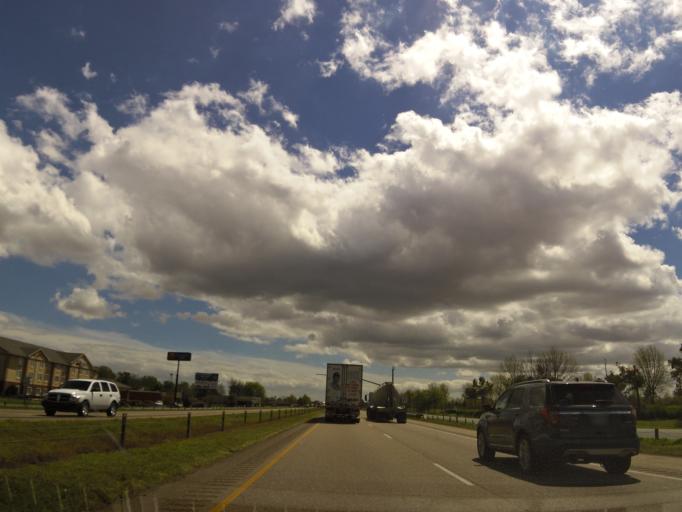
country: US
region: Arkansas
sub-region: Crittenden County
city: Marion
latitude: 35.2036
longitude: -90.2038
